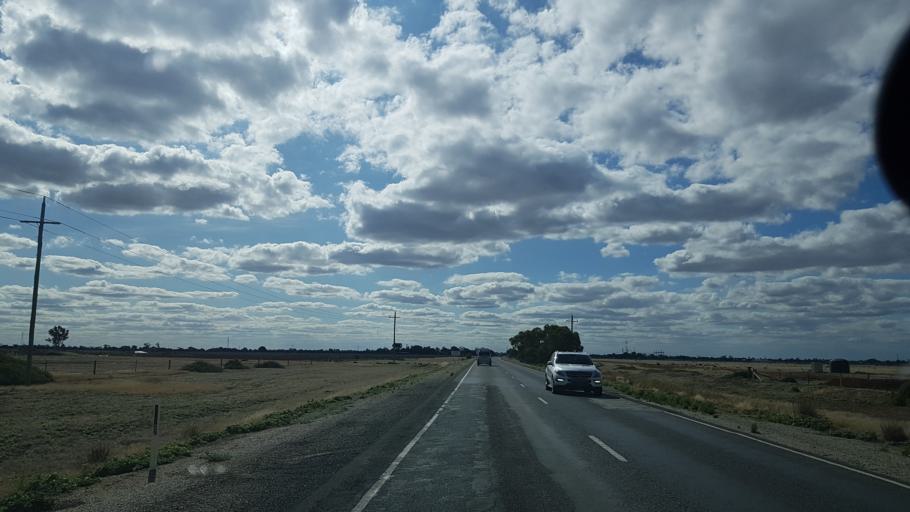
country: AU
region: Victoria
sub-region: Swan Hill
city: Swan Hill
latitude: -35.7903
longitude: 143.9457
